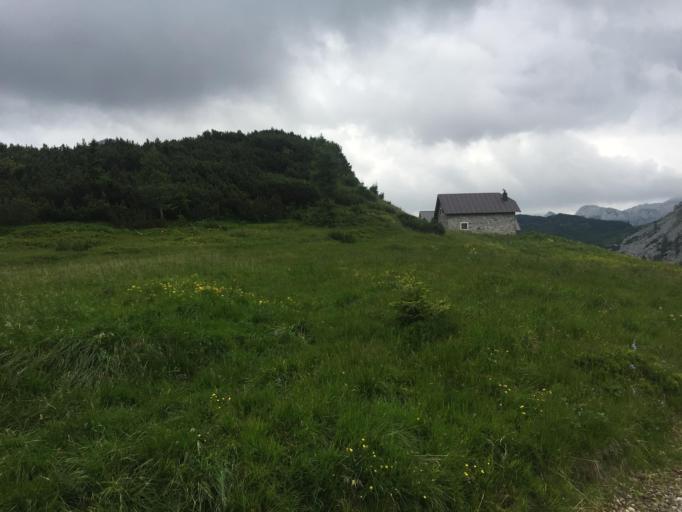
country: AT
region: Carinthia
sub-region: Politischer Bezirk Hermagor
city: Kirchbach
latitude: 46.5666
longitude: 13.1857
